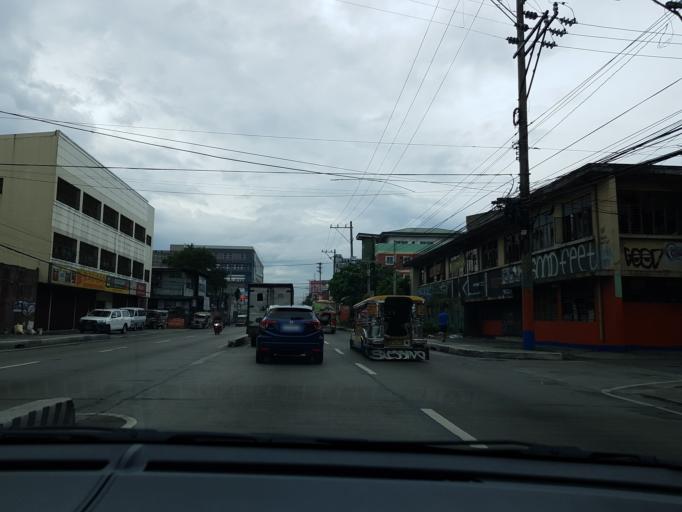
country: PH
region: Metro Manila
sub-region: Caloocan City
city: Niugan
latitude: 14.6619
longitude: 120.9841
